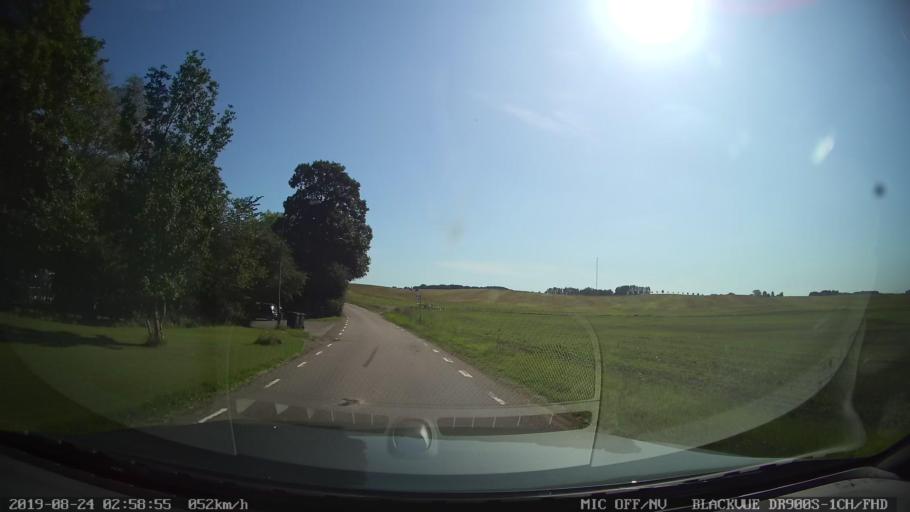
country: SE
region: Skane
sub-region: Skurups Kommun
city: Skurup
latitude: 55.4698
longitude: 13.4218
